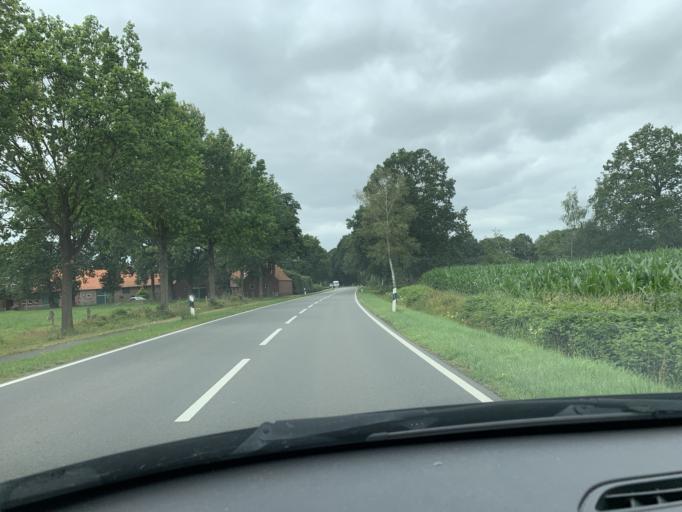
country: DE
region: Lower Saxony
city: Wiefelstede
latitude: 53.2081
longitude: 8.1043
